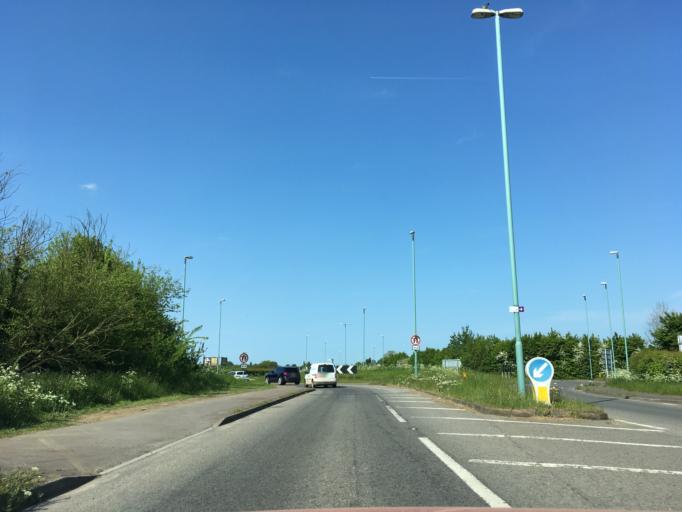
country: GB
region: England
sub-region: Gloucestershire
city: Dursley
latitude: 51.7229
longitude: -2.3728
